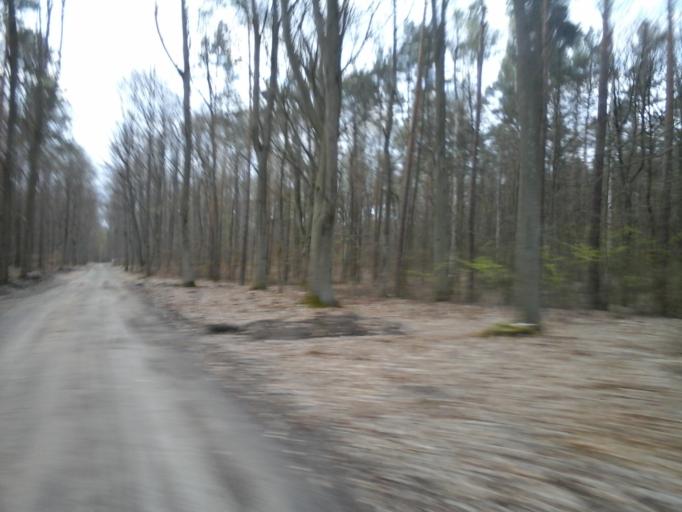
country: PL
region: West Pomeranian Voivodeship
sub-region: Powiat choszczenski
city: Bierzwnik
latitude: 53.0304
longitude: 15.6511
